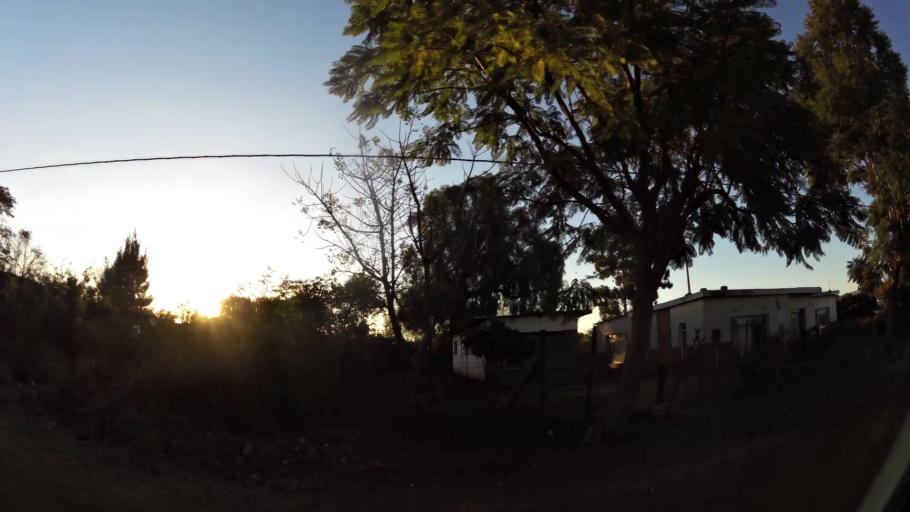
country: ZA
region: Limpopo
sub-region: Waterberg District Municipality
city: Mokopane
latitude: -24.1466
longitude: 28.9748
